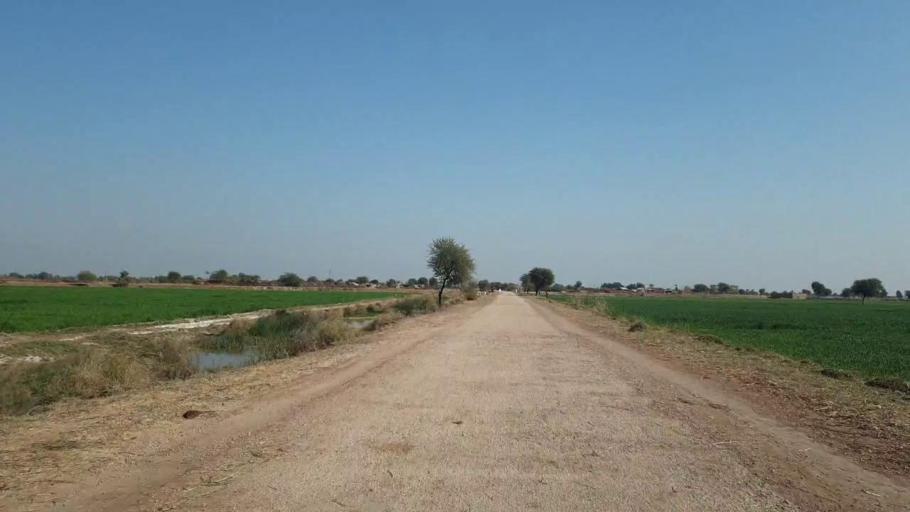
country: PK
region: Sindh
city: Shahdadpur
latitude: 25.9794
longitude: 68.6599
